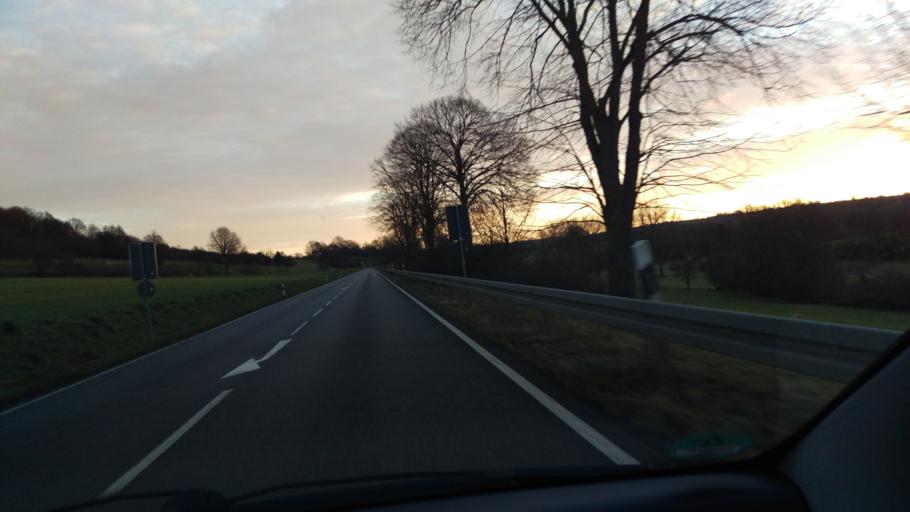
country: DE
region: Hesse
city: Kirtorf
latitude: 50.7537
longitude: 9.1389
